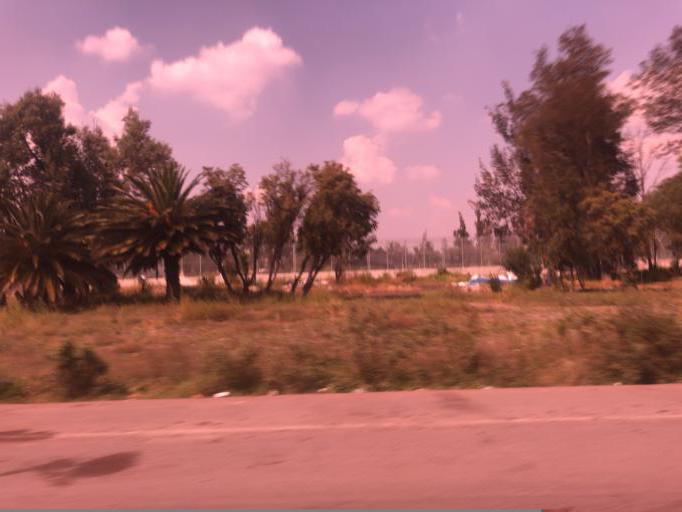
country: MX
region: Mexico
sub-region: Ciudad Nezahualcoyotl
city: Colonia Gustavo Baz Prada
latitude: 19.4725
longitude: -98.9961
